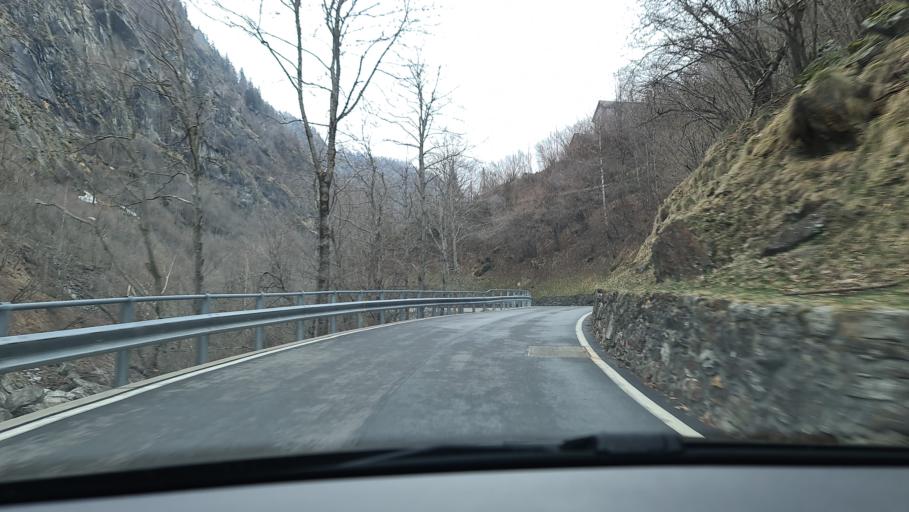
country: CH
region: Ticino
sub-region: Vallemaggia District
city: Cevio
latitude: 46.4154
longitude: 8.6506
